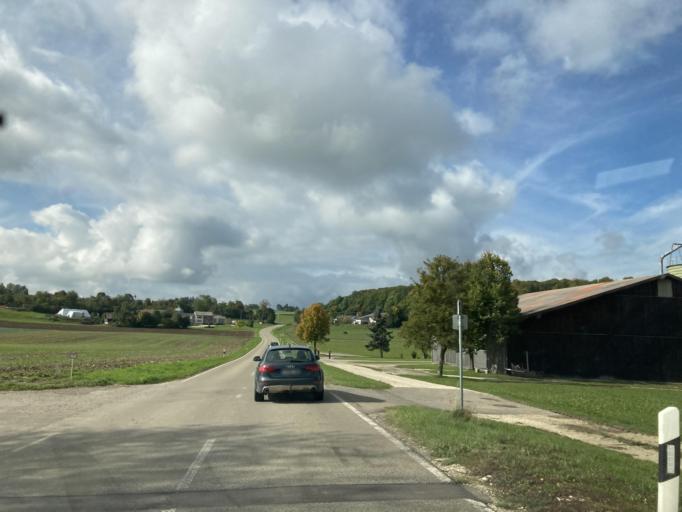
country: DE
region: Baden-Wuerttemberg
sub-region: Regierungsbezirk Stuttgart
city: Hohenstadt
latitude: 48.5398
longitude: 9.6838
